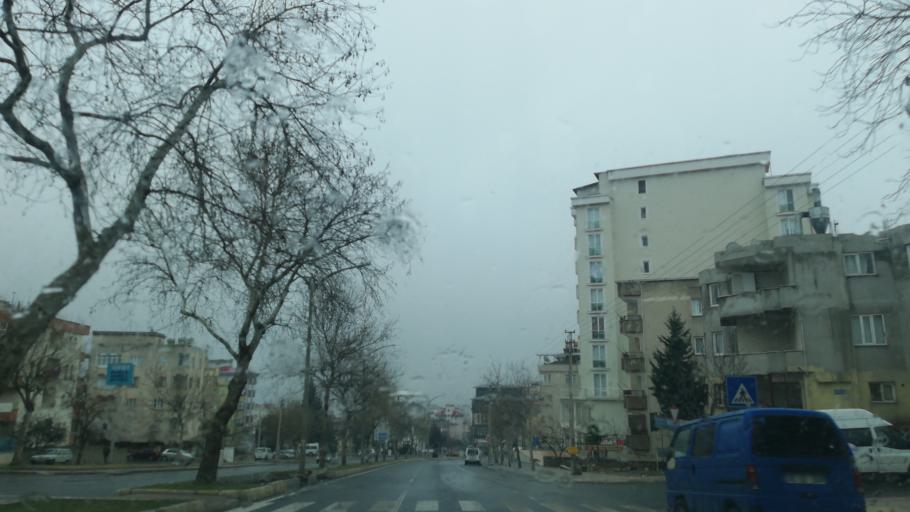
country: TR
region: Kahramanmaras
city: Kahramanmaras
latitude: 37.5910
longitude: 36.9015
